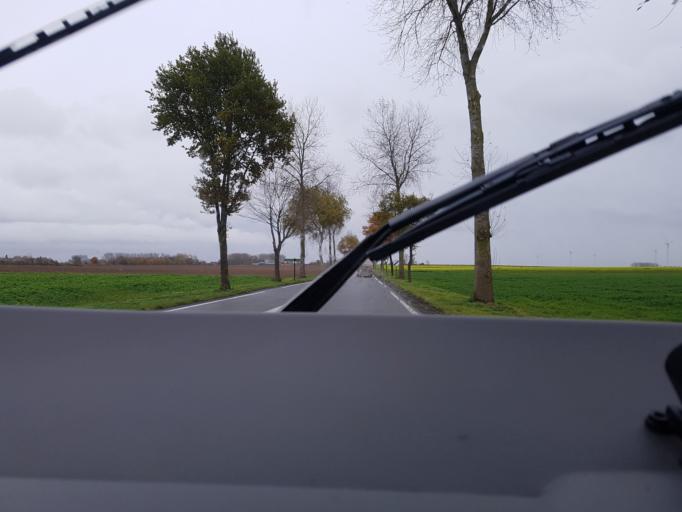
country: FR
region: Nord-Pas-de-Calais
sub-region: Departement du Pas-de-Calais
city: Savy-Berlette
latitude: 50.3594
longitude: 2.4613
